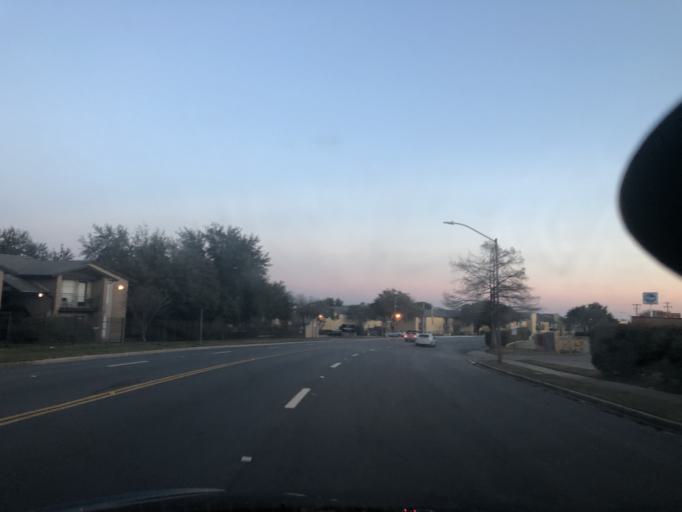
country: US
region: Texas
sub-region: Tarrant County
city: White Settlement
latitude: 32.7266
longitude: -97.4772
